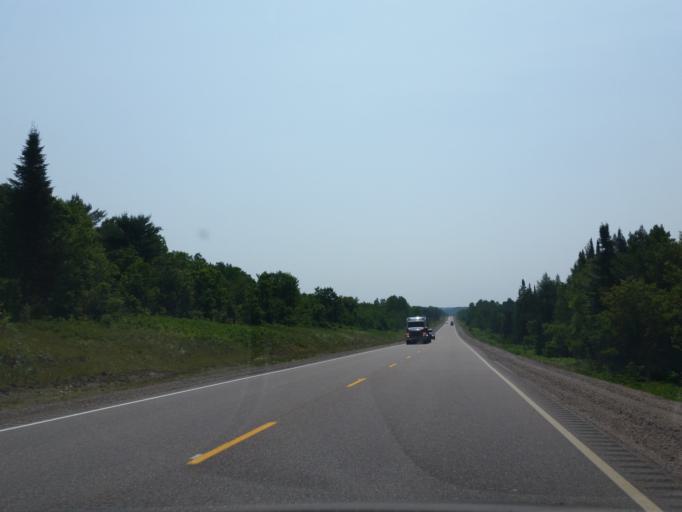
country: CA
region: Ontario
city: Mattawa
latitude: 46.2782
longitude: -78.3775
